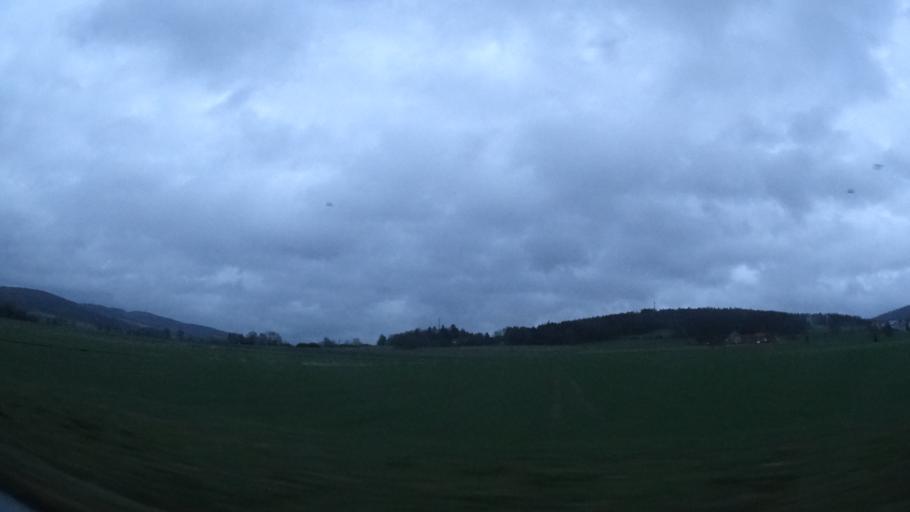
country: DE
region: Bavaria
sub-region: Regierungsbezirk Unterfranken
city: Motten
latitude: 50.4456
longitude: 9.7757
